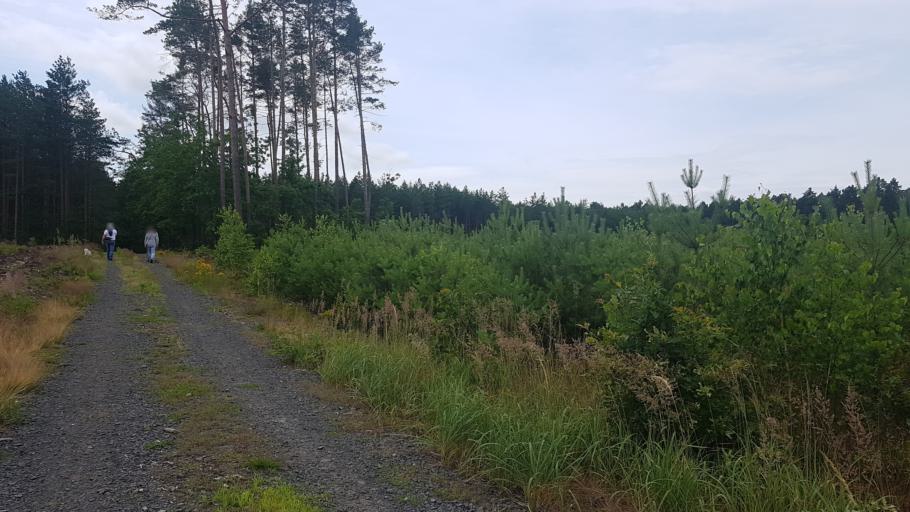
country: PL
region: Opole Voivodeship
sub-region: Powiat opolski
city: Chrzastowice
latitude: 50.7033
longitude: 18.1264
